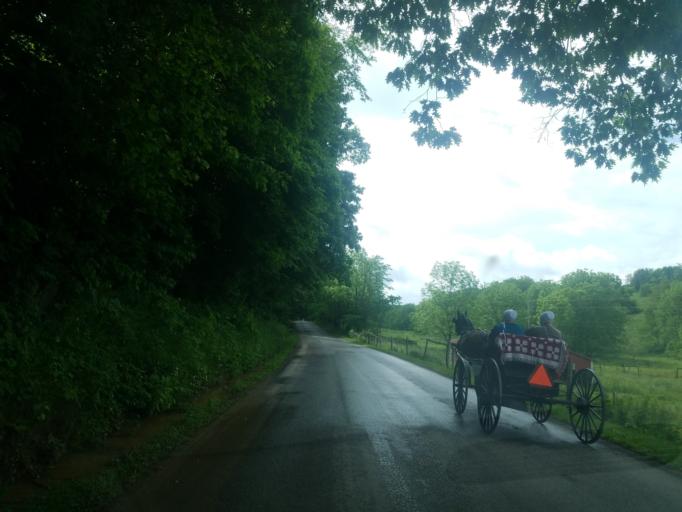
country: US
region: Ohio
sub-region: Holmes County
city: Millersburg
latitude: 40.4658
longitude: -81.8334
